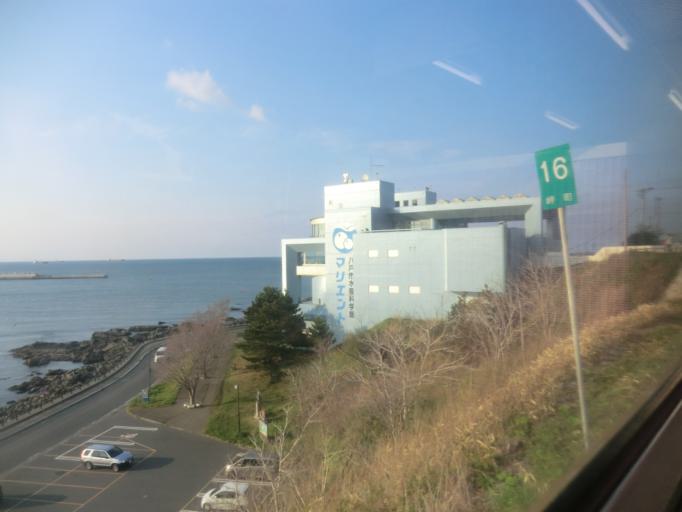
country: JP
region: Aomori
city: Hachinohe
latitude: 40.5391
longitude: 141.5623
